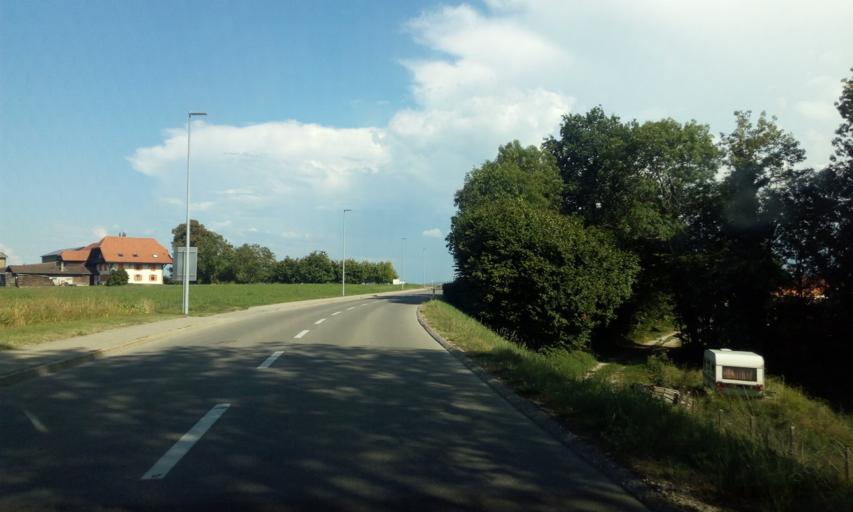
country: CH
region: Fribourg
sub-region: Broye District
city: Domdidier
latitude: 46.9128
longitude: 6.9706
